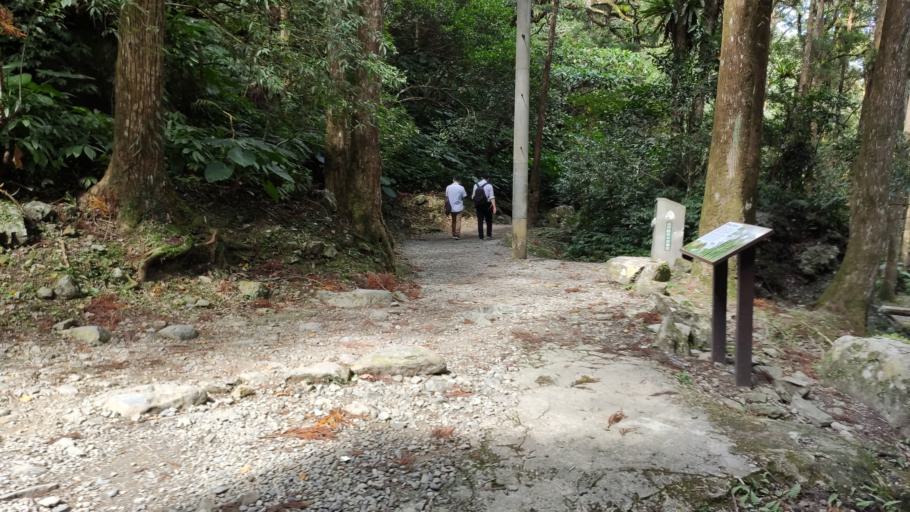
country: TW
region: Taiwan
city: Daxi
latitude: 24.8204
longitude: 121.4500
